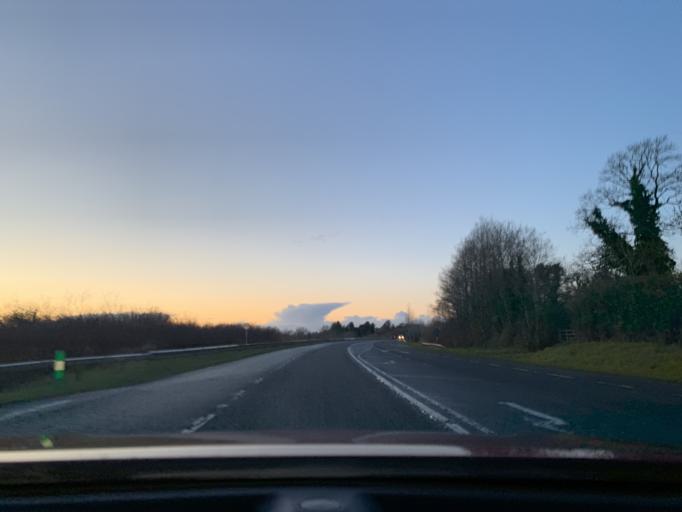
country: IE
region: Connaught
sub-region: County Leitrim
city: Carrick-on-Shannon
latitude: 53.9335
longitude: -8.0436
